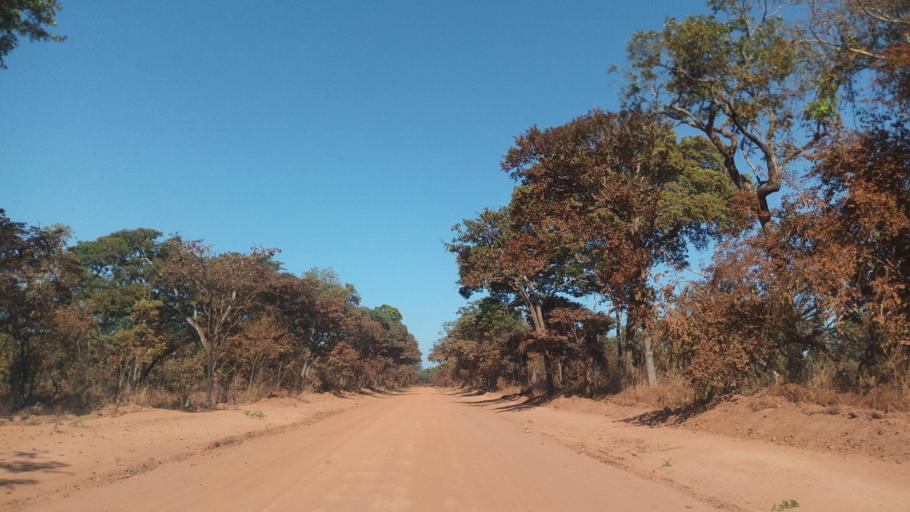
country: ZM
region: Luapula
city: Mwense
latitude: -10.7411
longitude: 28.3305
